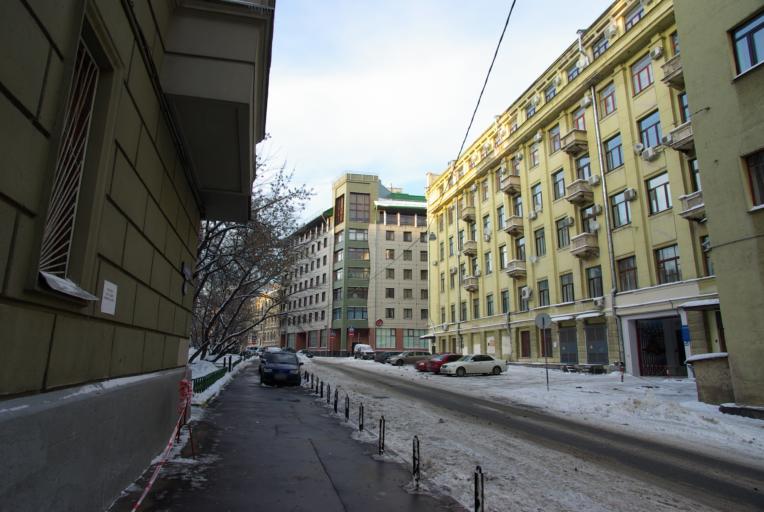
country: RU
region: Moscow
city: Moscow
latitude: 55.7688
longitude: 37.6408
